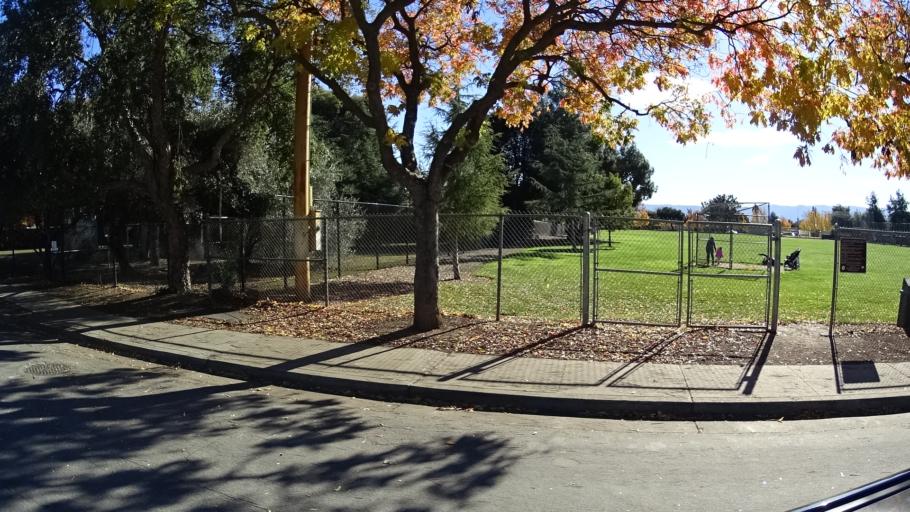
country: US
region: California
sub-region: Santa Clara County
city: Sunnyvale
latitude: 37.3487
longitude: -122.0183
